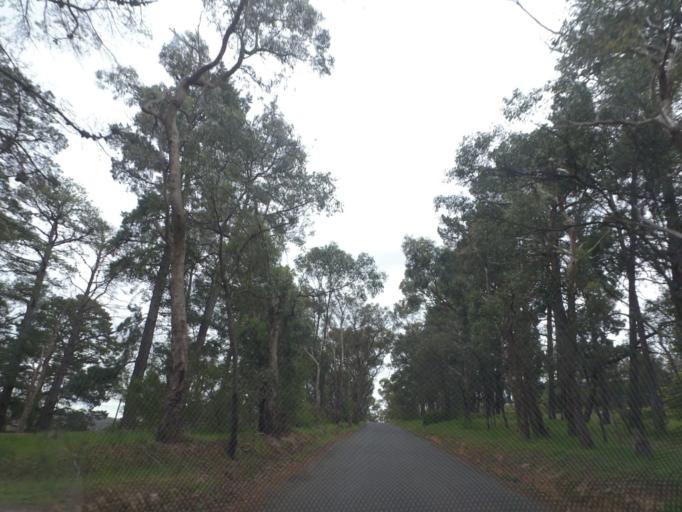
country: AU
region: Victoria
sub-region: Nillumbik
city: Hurstbridge
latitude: -37.6633
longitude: 145.2148
